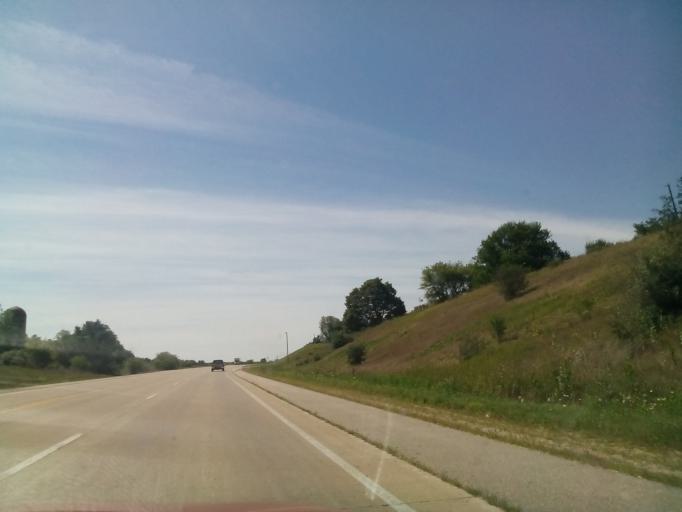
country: US
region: Wisconsin
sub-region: Green County
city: Monroe
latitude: 42.6330
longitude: -89.6317
